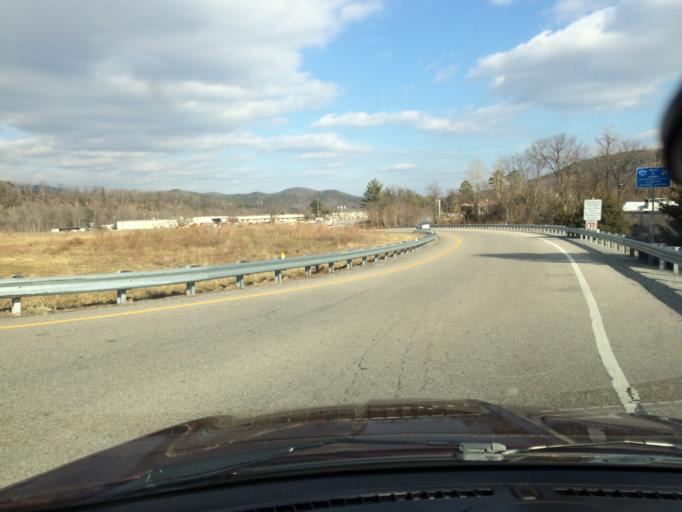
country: US
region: Virginia
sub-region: Alleghany County
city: Clifton Forge
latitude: 37.7913
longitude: -79.8856
